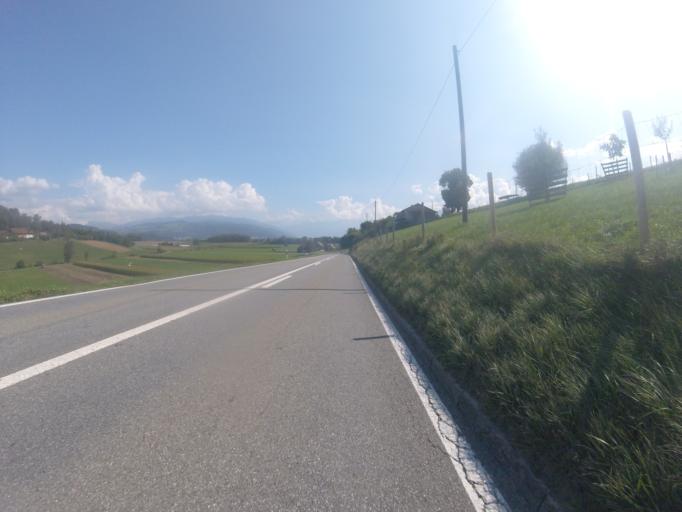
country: CH
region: Bern
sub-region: Thun District
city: Seftigen
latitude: 46.7905
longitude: 7.5581
